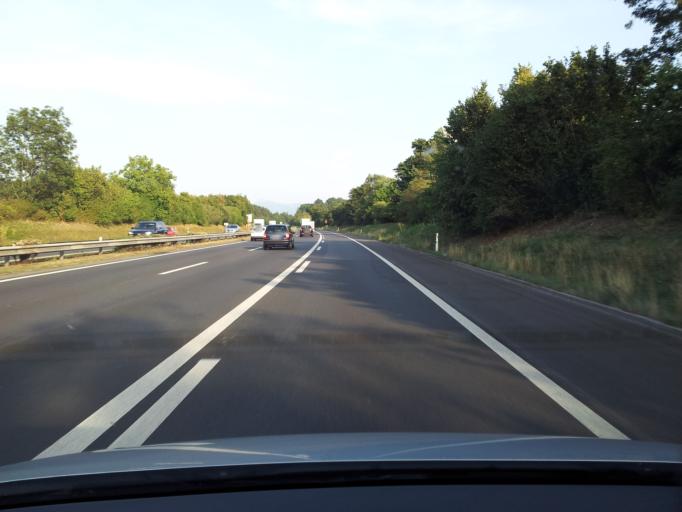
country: CH
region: Lucerne
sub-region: Sursee District
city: Sempach
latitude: 47.1352
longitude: 8.2022
